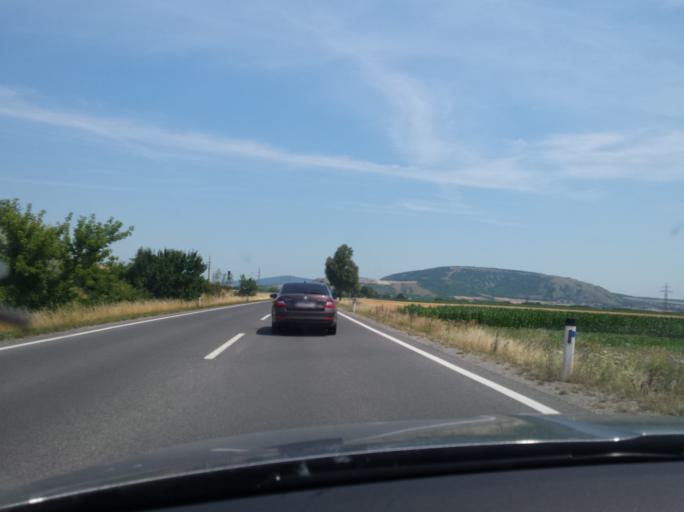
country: AT
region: Lower Austria
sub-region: Politischer Bezirk Bruck an der Leitha
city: Petronell-Carnuntum
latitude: 48.1090
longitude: 16.8754
